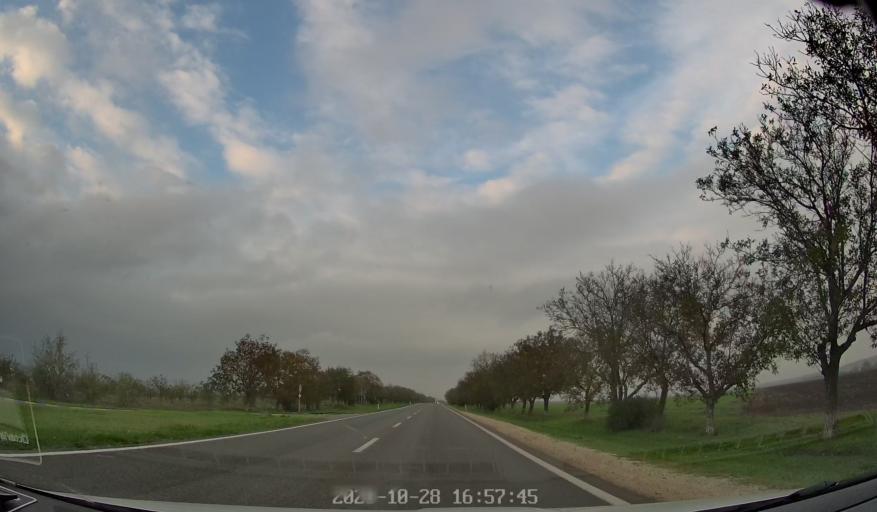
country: MD
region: Gagauzia
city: Bugeac
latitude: 46.3689
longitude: 28.6812
